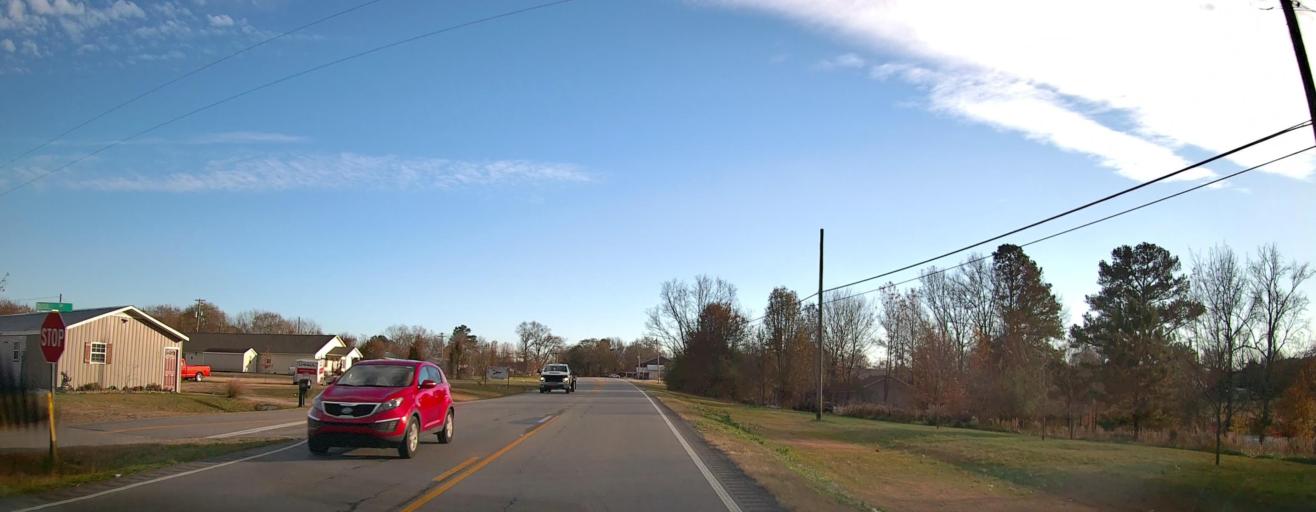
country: US
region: Alabama
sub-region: Marshall County
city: Arab
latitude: 34.3142
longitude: -86.6000
